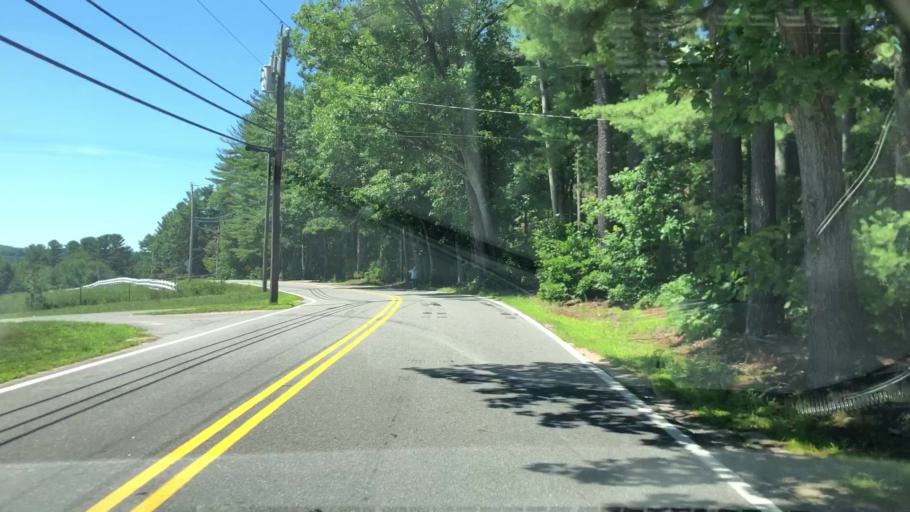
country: US
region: New Hampshire
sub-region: Hillsborough County
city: Milford
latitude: 42.8380
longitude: -71.6071
